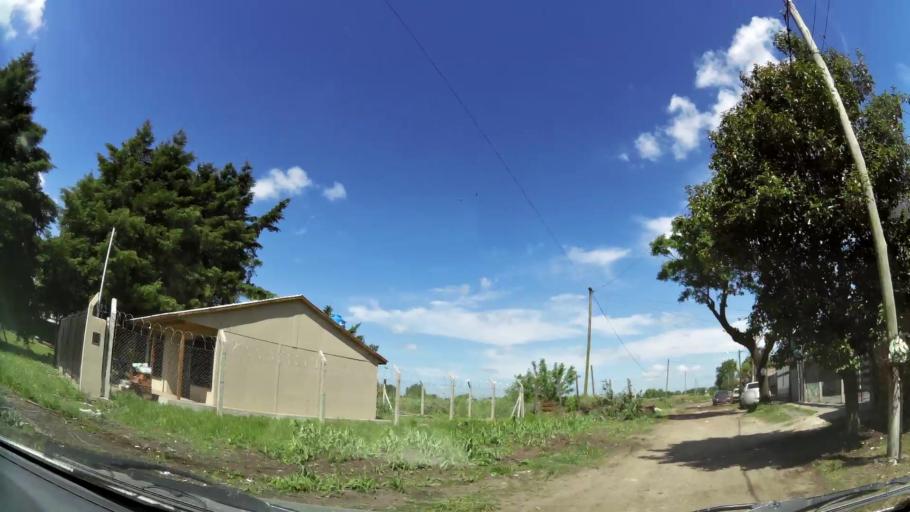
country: AR
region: Buenos Aires
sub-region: Partido de Quilmes
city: Quilmes
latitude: -34.8229
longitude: -58.2680
